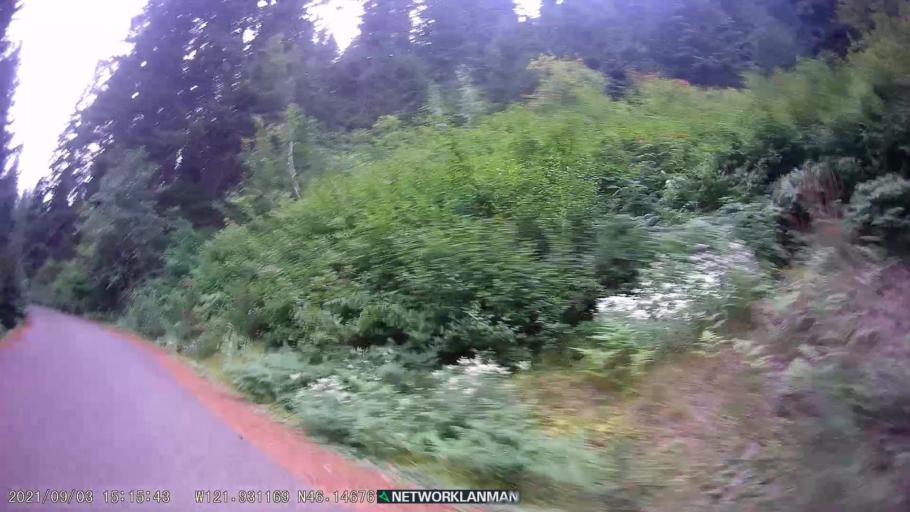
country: US
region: Washington
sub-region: Skamania County
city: Carson
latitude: 46.1468
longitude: -121.9311
